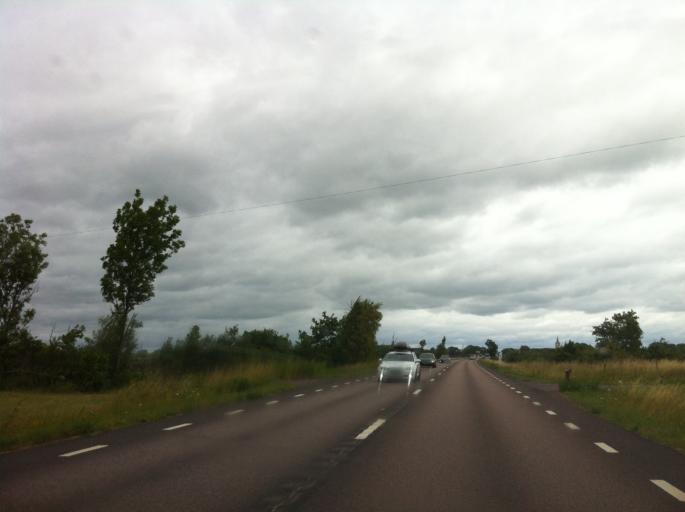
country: SE
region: Kalmar
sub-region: Borgholms Kommun
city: Borgholm
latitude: 57.1143
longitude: 16.9549
